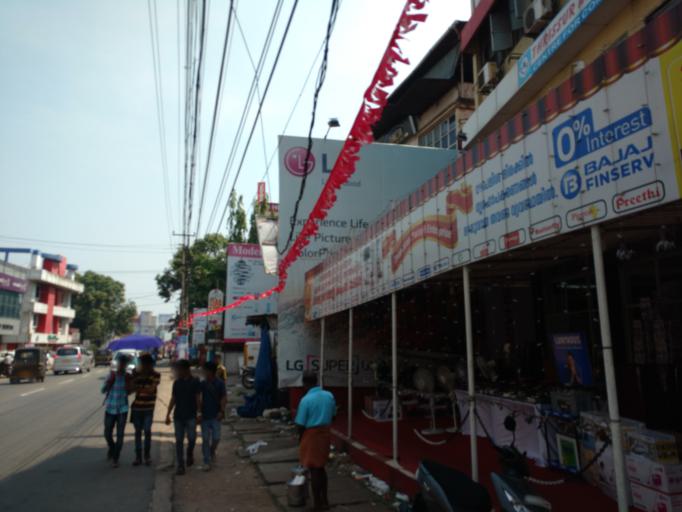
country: IN
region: Kerala
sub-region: Thrissur District
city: Trichur
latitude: 10.5228
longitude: 76.2054
